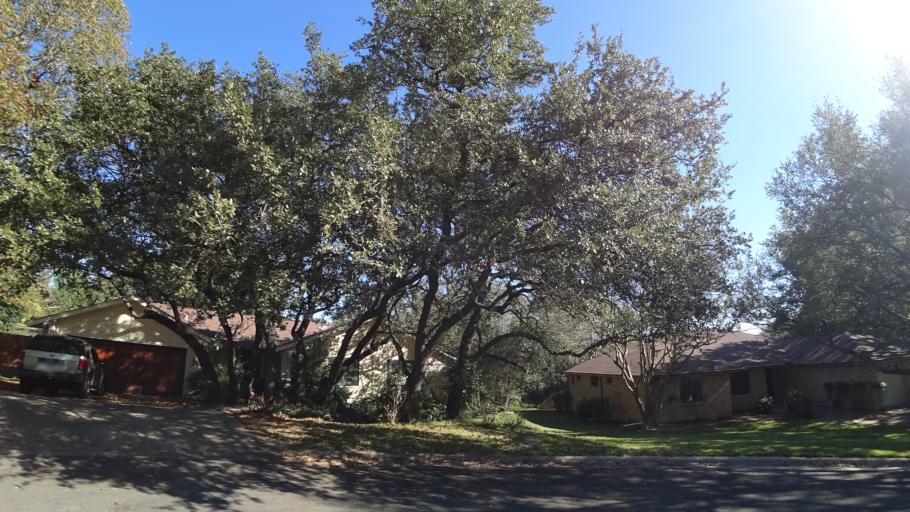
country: US
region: Texas
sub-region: Williamson County
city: Jollyville
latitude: 30.4167
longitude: -97.7678
